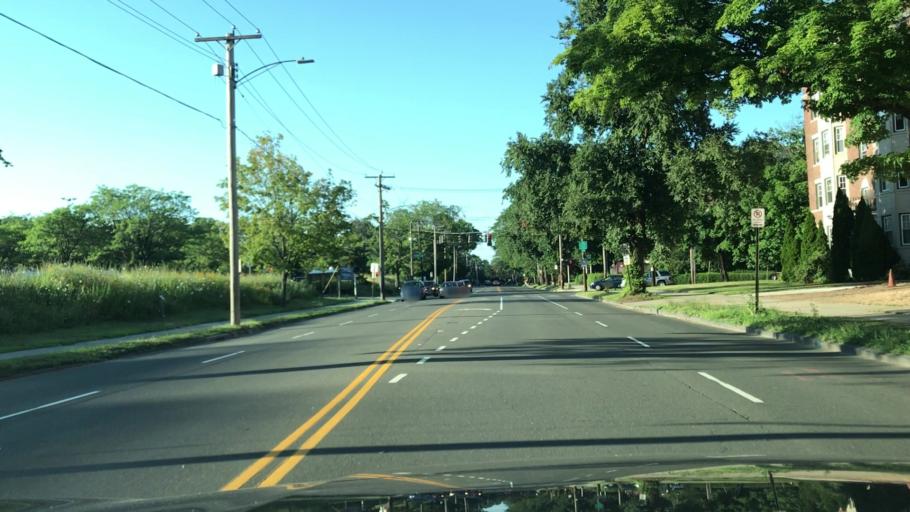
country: US
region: Connecticut
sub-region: New Haven County
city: New Haven
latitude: 41.3170
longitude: -72.9201
